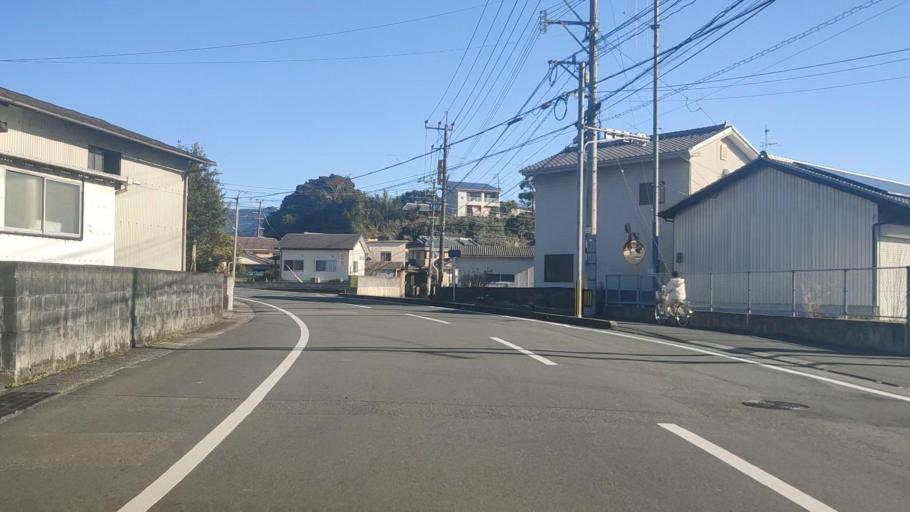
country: JP
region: Miyazaki
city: Nobeoka
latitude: 32.6097
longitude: 131.6883
